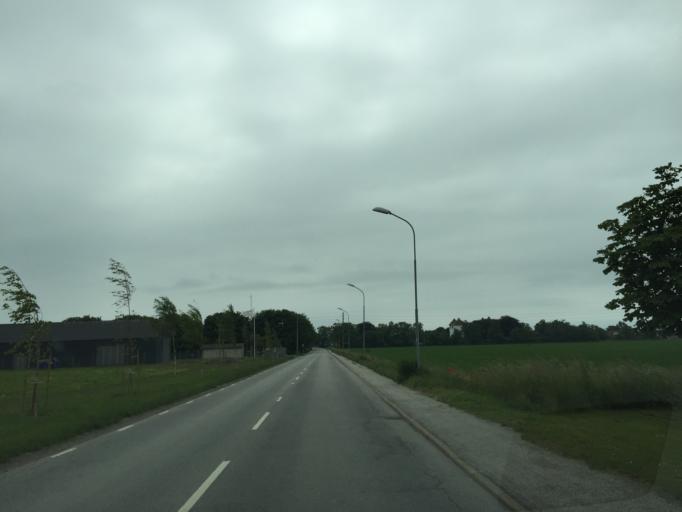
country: SE
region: Skane
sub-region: Ystads Kommun
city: Kopingebro
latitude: 55.4326
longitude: 14.1133
